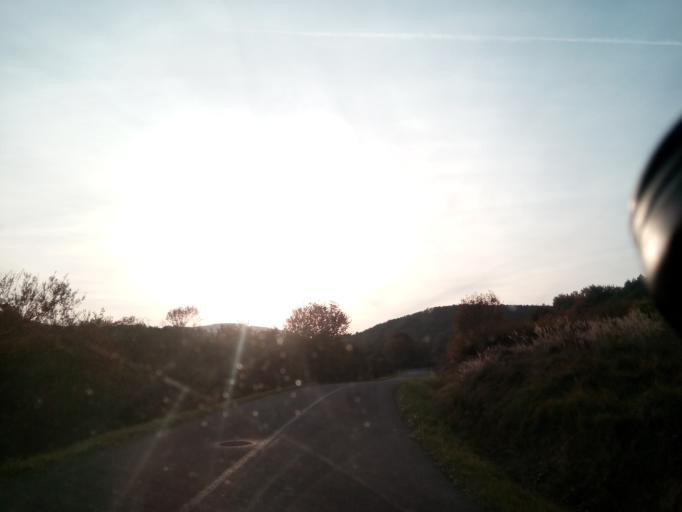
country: SK
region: Presovsky
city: Svidnik
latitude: 49.3550
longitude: 21.4720
